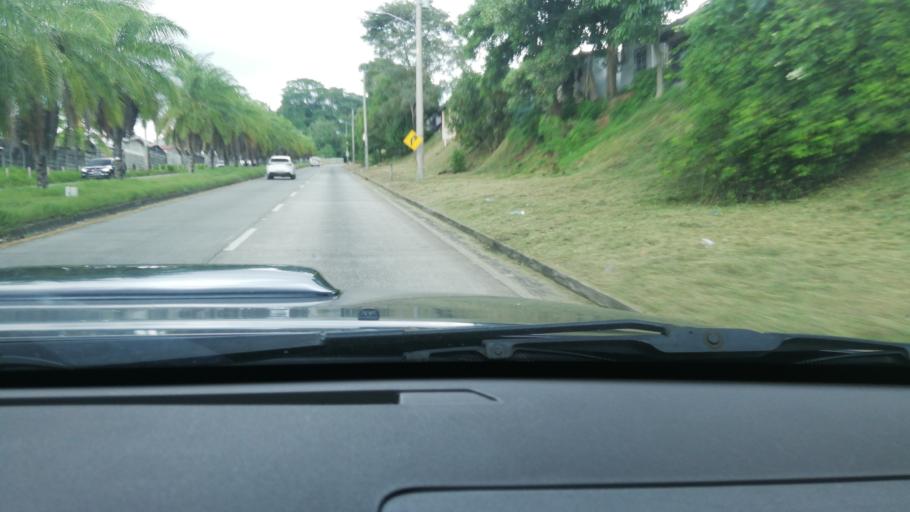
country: PA
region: Panama
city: San Miguelito
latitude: 9.0471
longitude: -79.4838
